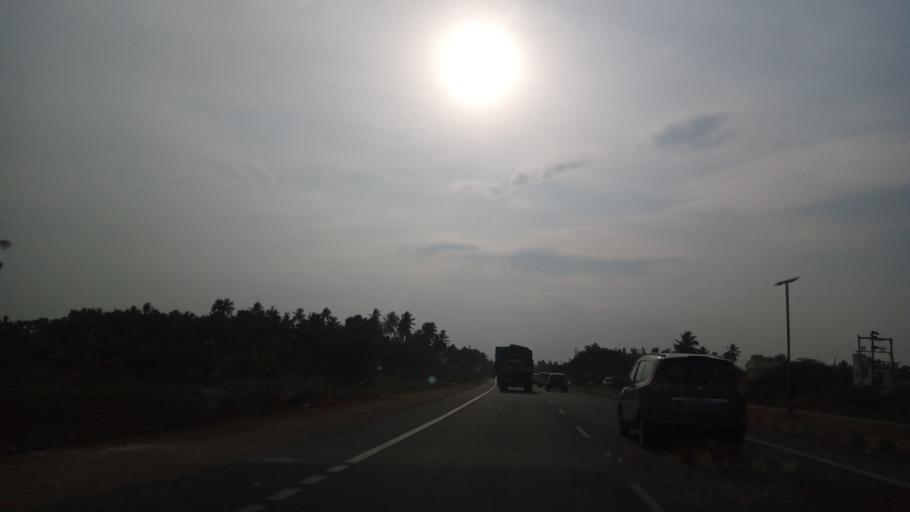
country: IN
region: Tamil Nadu
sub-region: Salem
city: Belur
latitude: 11.6505
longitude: 78.4983
